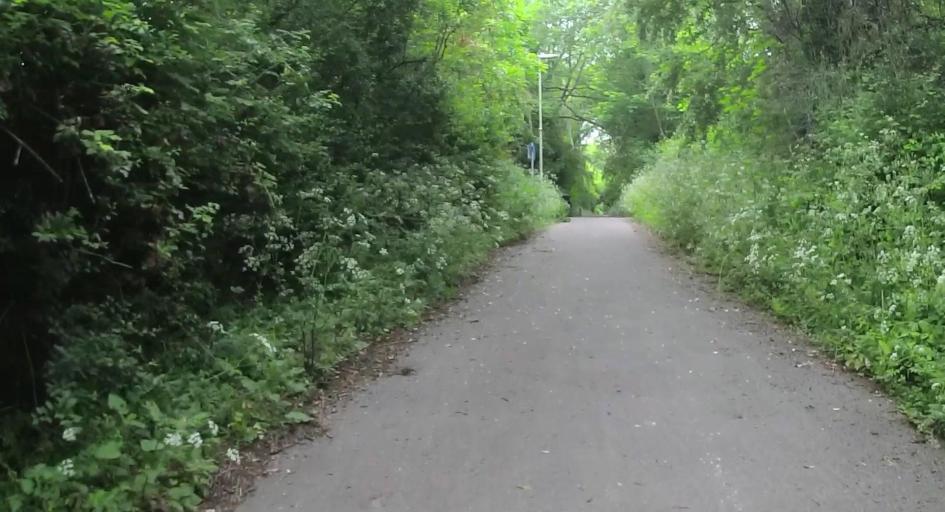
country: GB
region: England
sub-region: Hampshire
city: Basingstoke
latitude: 51.2646
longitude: -1.1226
